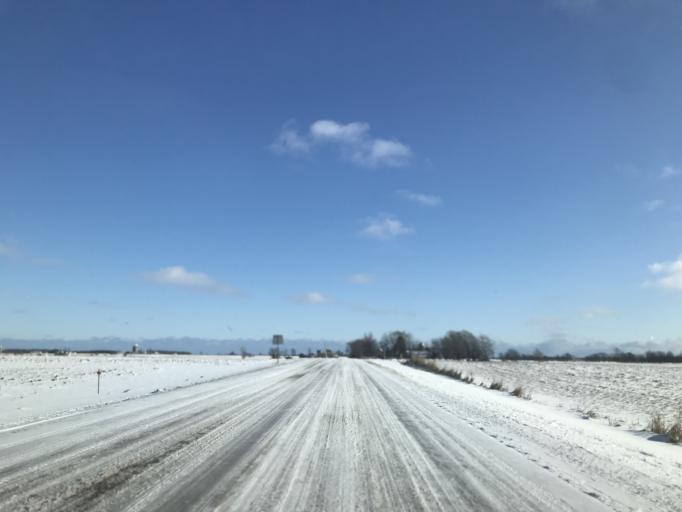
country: US
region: Wisconsin
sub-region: Kewaunee County
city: Luxemburg
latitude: 44.6978
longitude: -87.6189
